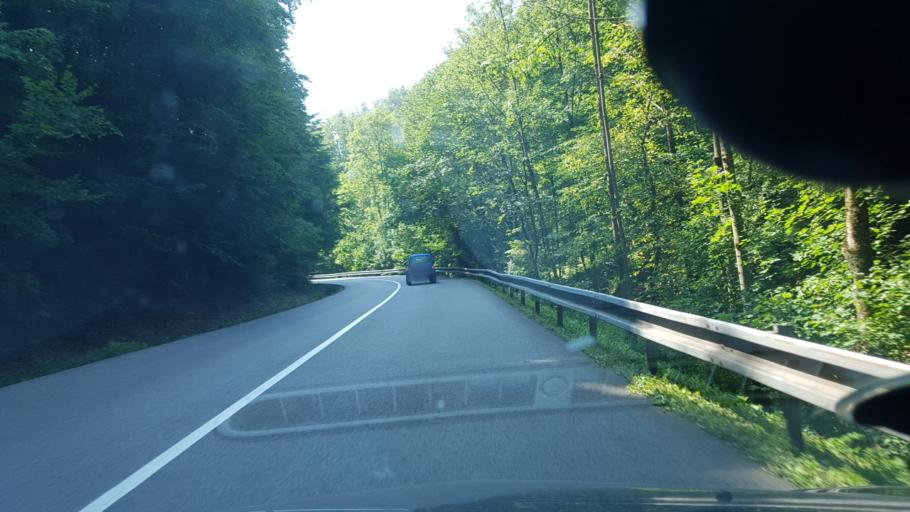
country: SK
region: Banskobystricky
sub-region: Okres Banska Bystrica
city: Banska Bystrica
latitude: 48.7194
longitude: 19.1670
